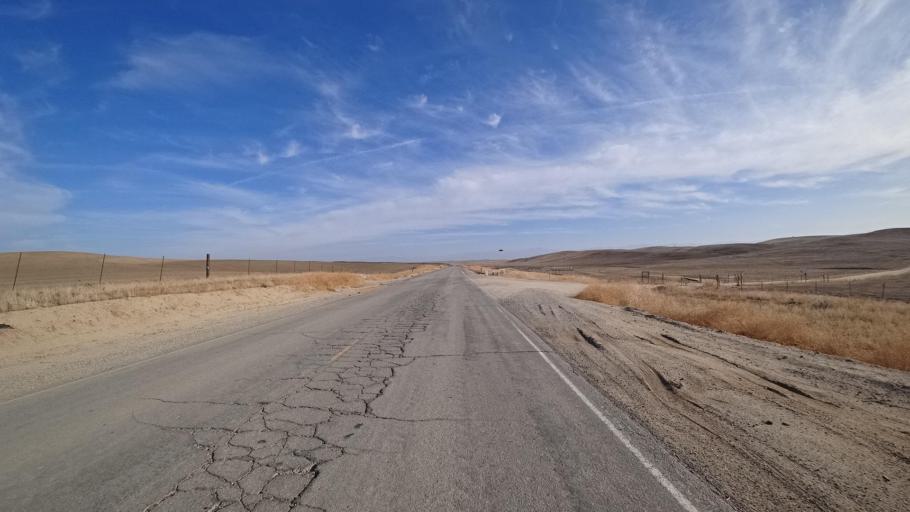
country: US
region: California
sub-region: Kern County
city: McFarland
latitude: 35.6084
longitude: -119.0620
